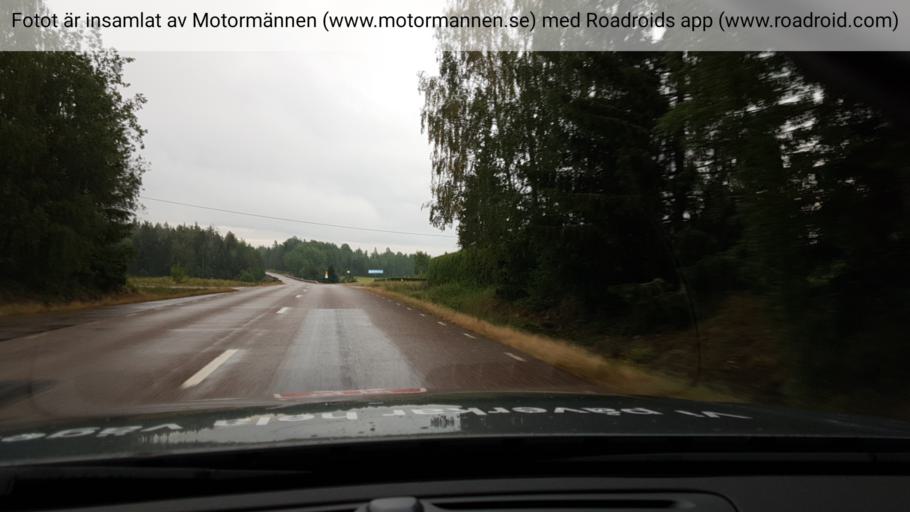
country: SE
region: Dalarna
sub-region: Avesta Kommun
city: Avesta
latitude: 59.9667
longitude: 16.1803
